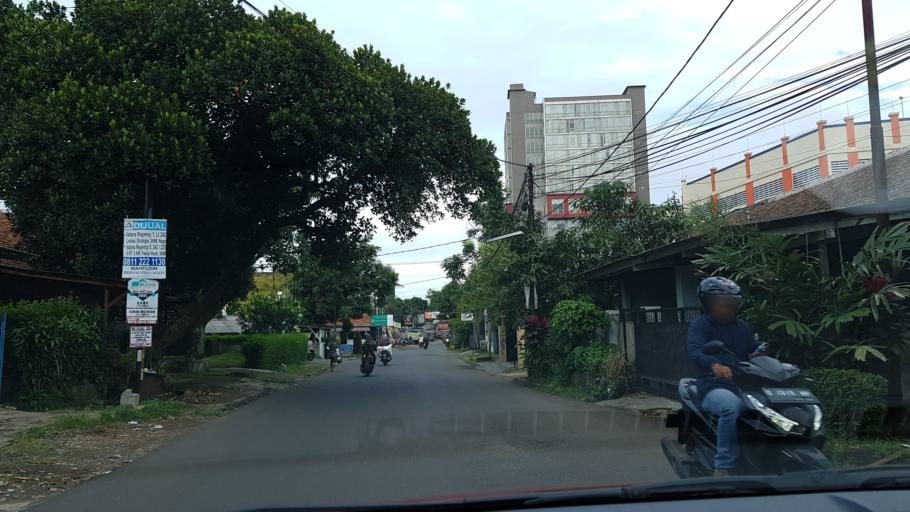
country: ID
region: West Java
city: Bandung
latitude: -6.8942
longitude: 107.5862
